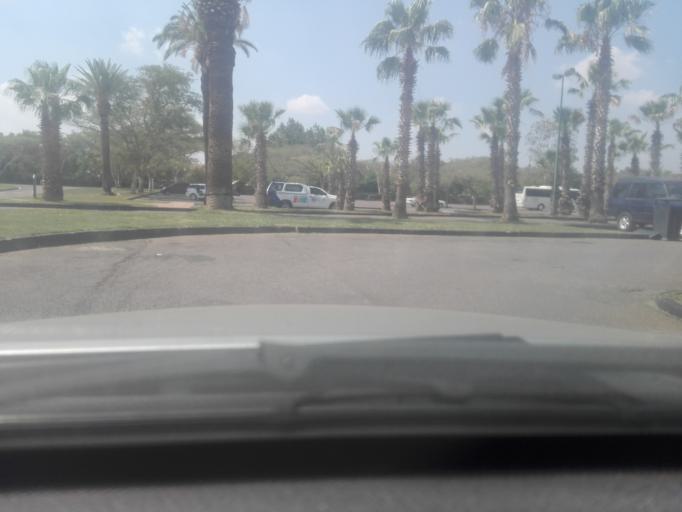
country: BW
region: Kweneng
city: Mogoditshane
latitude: -24.6398
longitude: 25.8777
